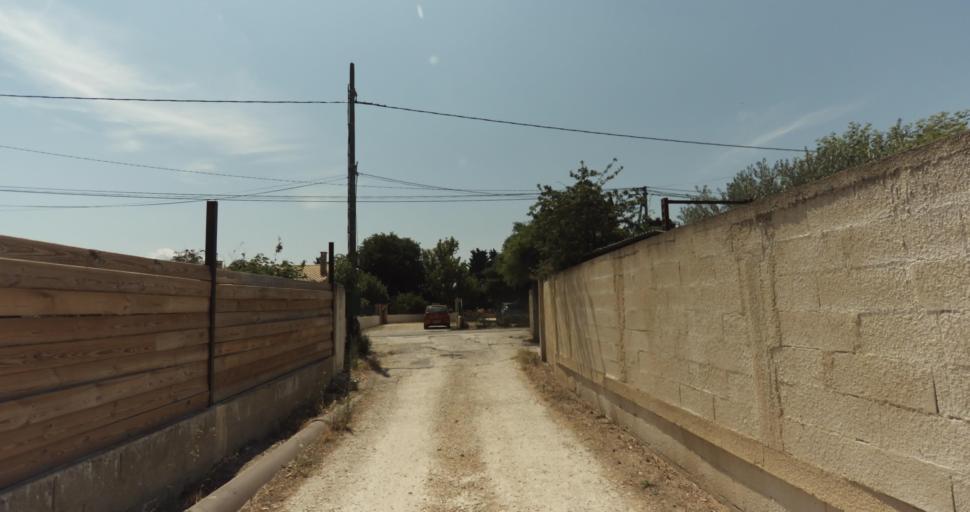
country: FR
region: Provence-Alpes-Cote d'Azur
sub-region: Departement du Vaucluse
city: Monteux
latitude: 44.0284
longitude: 4.9826
